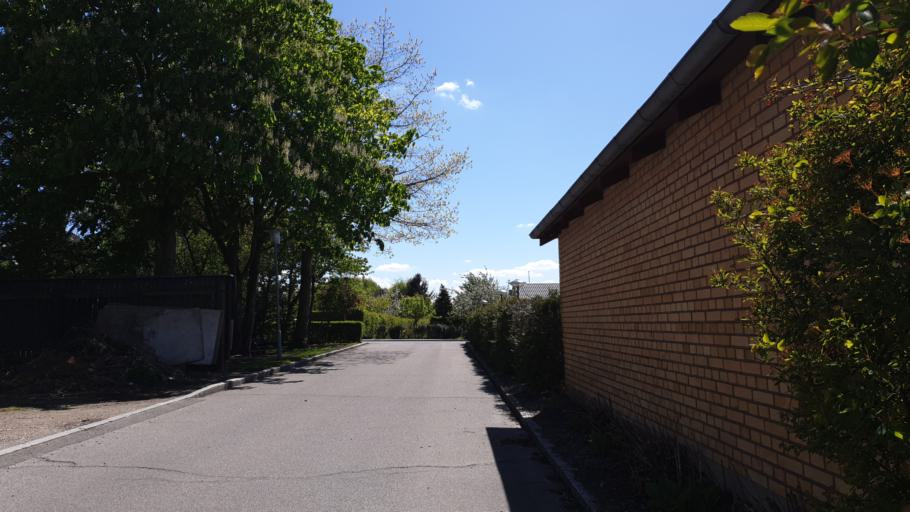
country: DK
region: Central Jutland
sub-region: Hedensted Kommune
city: Hedensted
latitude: 55.8018
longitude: 9.7002
